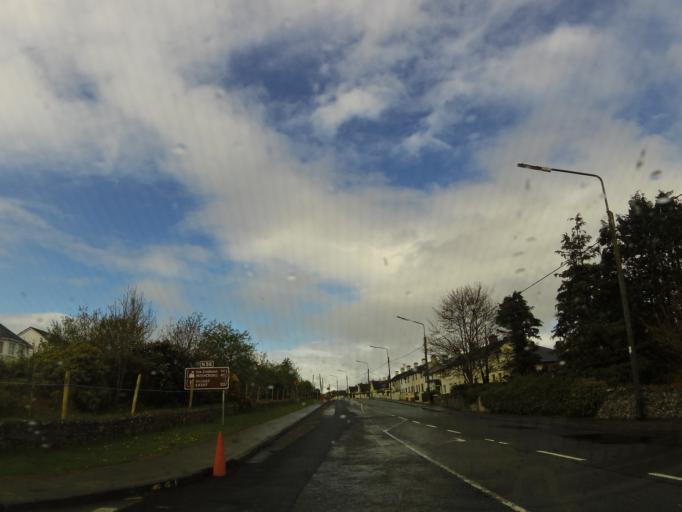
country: IE
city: Ballisodare
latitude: 54.2105
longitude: -8.5142
